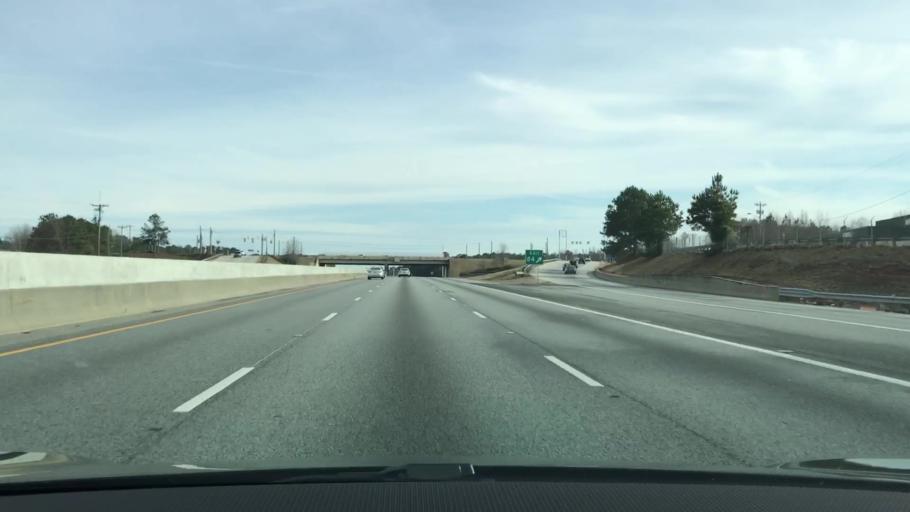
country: US
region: Georgia
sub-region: Rockdale County
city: Conyers
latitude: 33.6375
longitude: -83.9808
